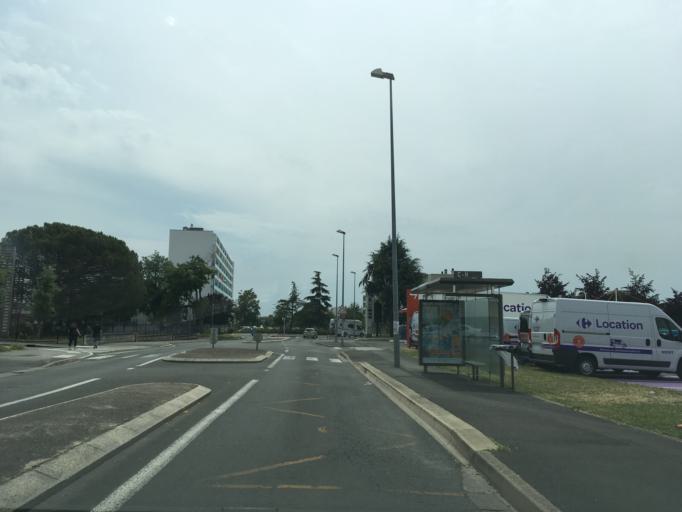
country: FR
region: Poitou-Charentes
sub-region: Departement des Deux-Sevres
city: Niort
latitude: 46.3178
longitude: -0.4802
